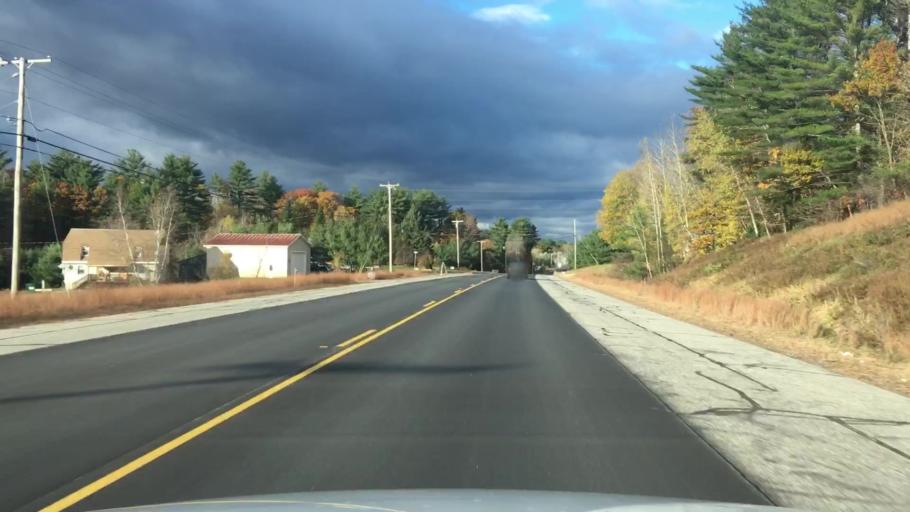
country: US
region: Maine
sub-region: Androscoggin County
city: Livermore
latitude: 44.3573
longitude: -70.2559
